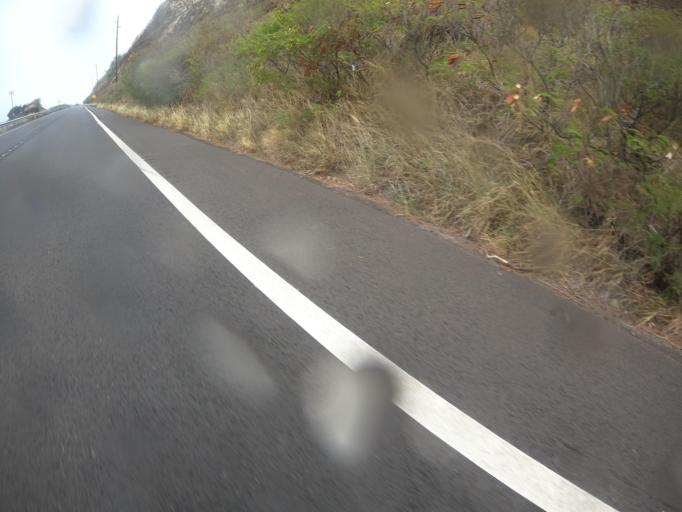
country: US
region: Hawaii
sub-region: Honolulu County
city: Makaha Valley
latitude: 21.5397
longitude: -158.2337
